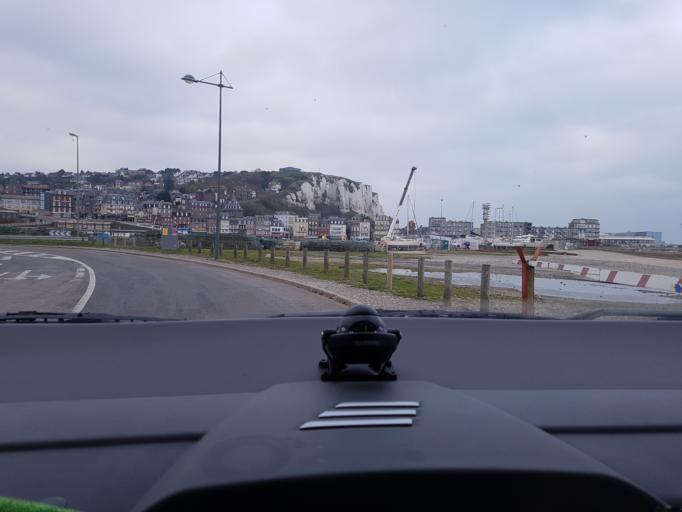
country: FR
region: Haute-Normandie
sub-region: Departement de la Seine-Maritime
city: Le Treport
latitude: 50.0629
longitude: 1.3754
